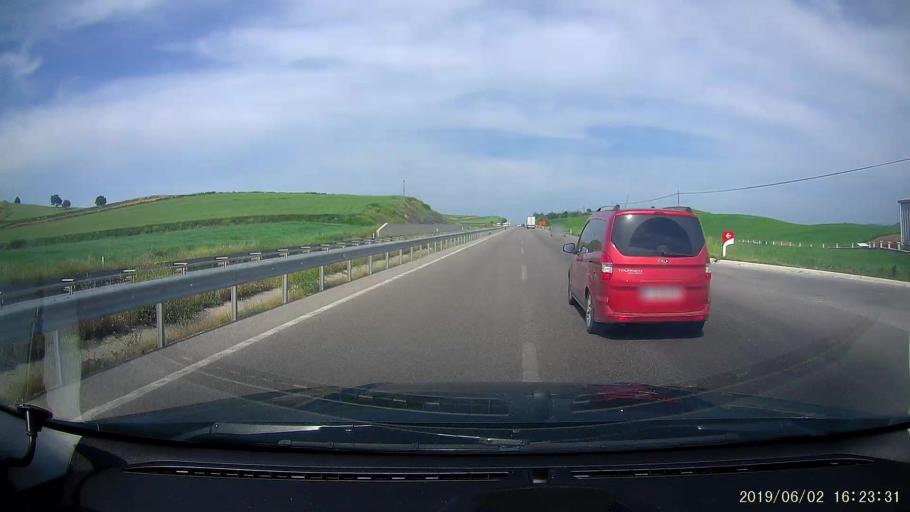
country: TR
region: Samsun
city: Havza
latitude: 40.9947
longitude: 35.7378
